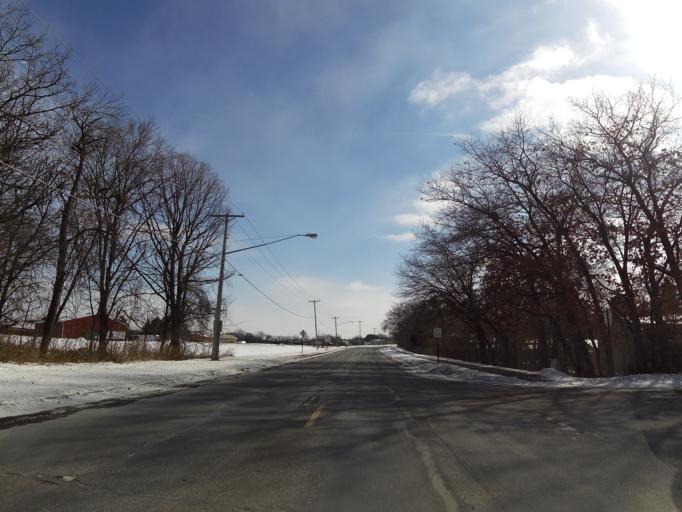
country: US
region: Minnesota
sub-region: Ramsey County
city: Maplewood
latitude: 44.9378
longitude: -92.9780
